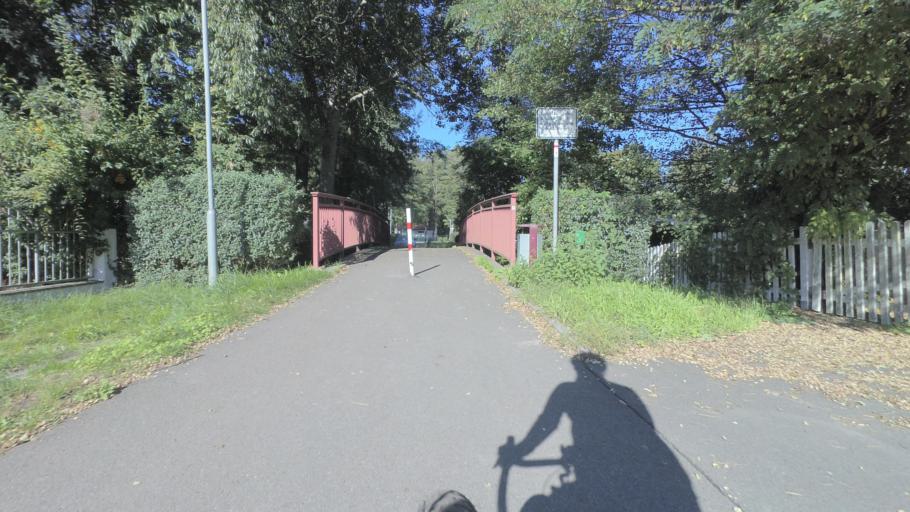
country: DE
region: Brandenburg
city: Rangsdorf
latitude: 52.2879
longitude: 13.4155
